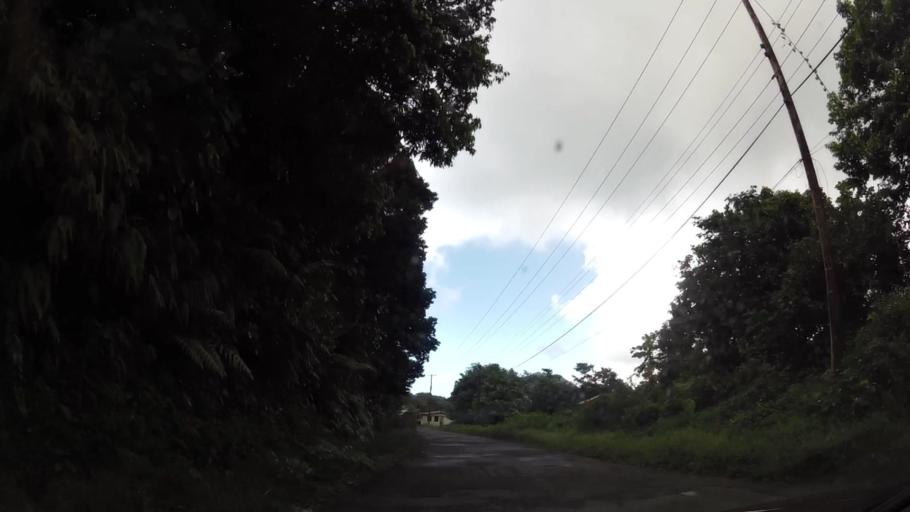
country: DM
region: Saint Paul
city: Pont Casse
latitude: 15.3925
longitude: -61.3160
